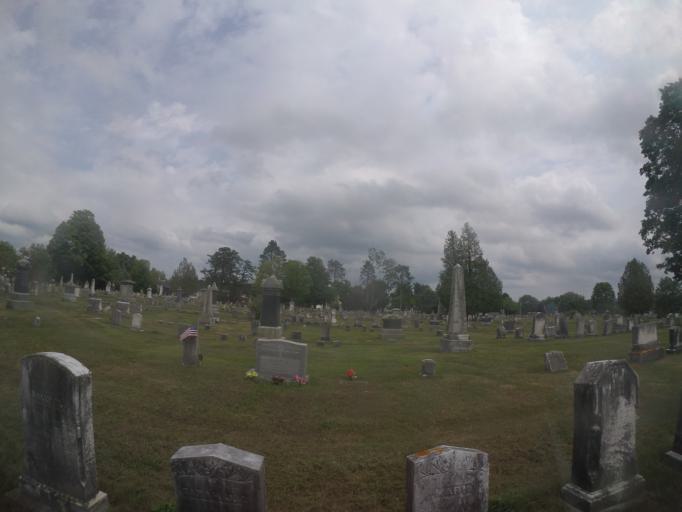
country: US
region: Maine
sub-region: Cumberland County
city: New Gloucester
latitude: 43.8857
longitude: -70.3330
